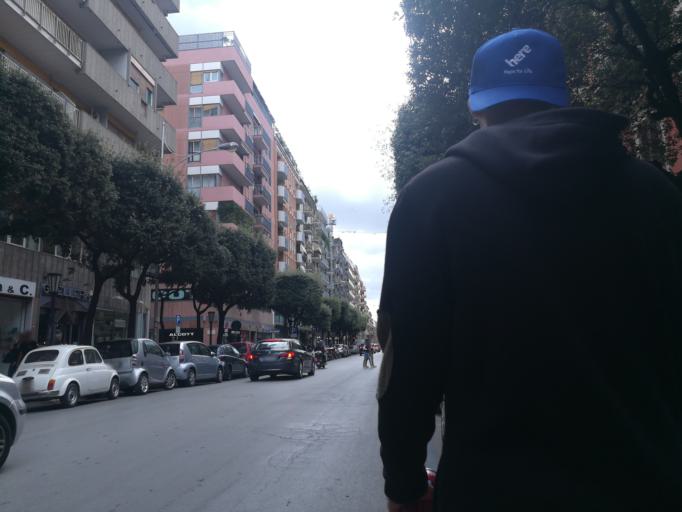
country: IT
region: Apulia
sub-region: Provincia di Bari
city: Bari
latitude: 41.1212
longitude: 16.8725
